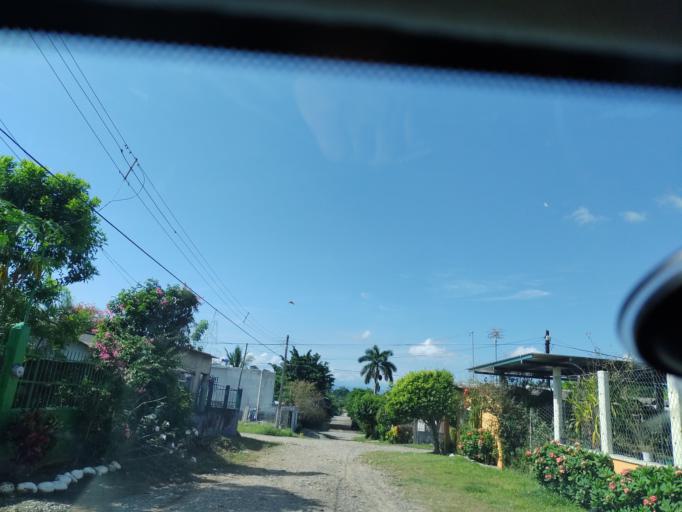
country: MX
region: Veracruz
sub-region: Martinez de la Torre
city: El Progreso
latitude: 20.1153
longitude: -97.0124
